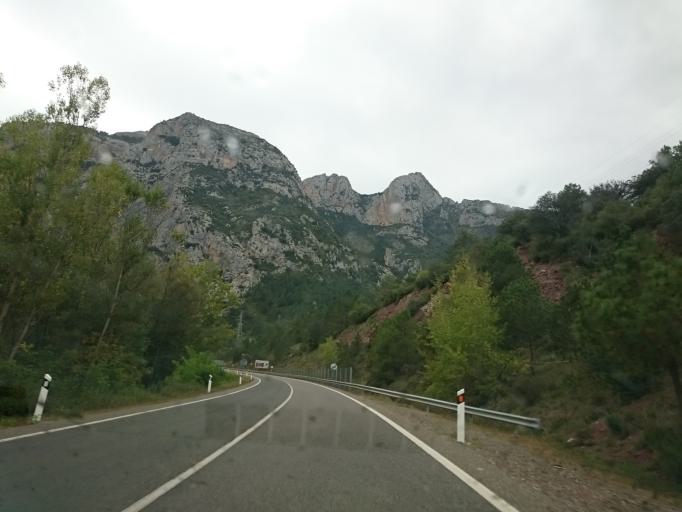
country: ES
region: Catalonia
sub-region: Provincia de Lleida
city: Senterada
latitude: 42.3022
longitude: 1.0394
